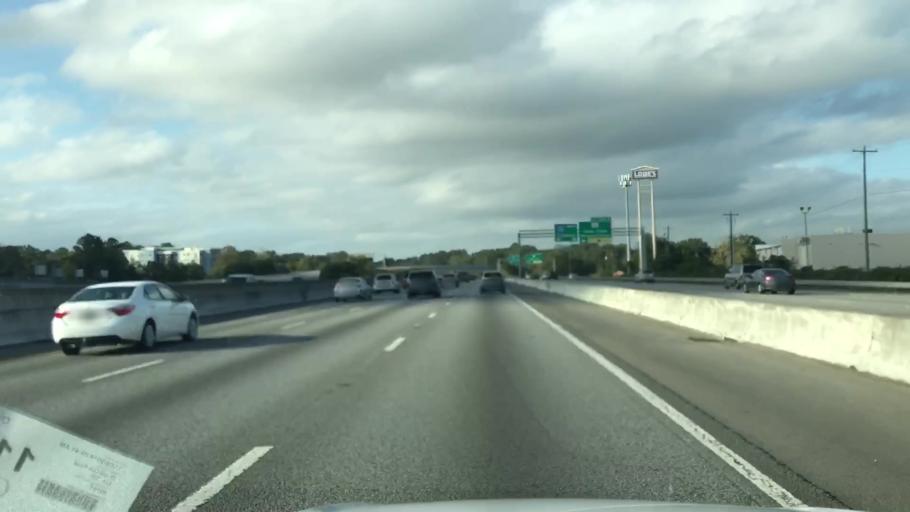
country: US
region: South Carolina
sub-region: Berkeley County
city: Hanahan
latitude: 32.9363
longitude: -80.0482
